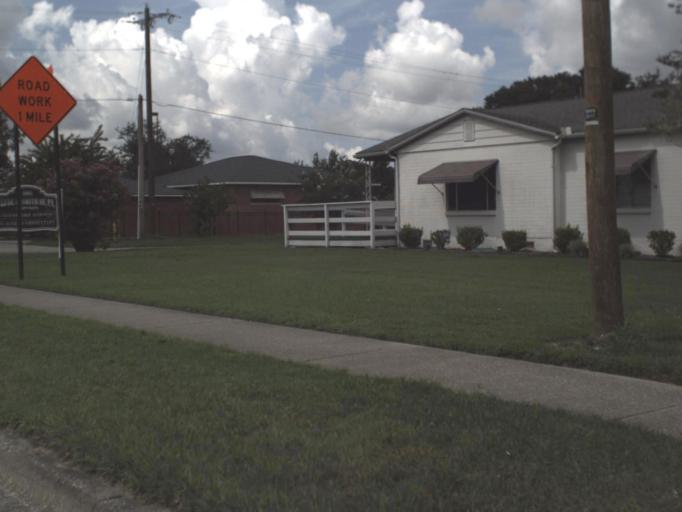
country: US
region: Florida
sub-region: Hillsborough County
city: Plant City
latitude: 27.9990
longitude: -82.1215
